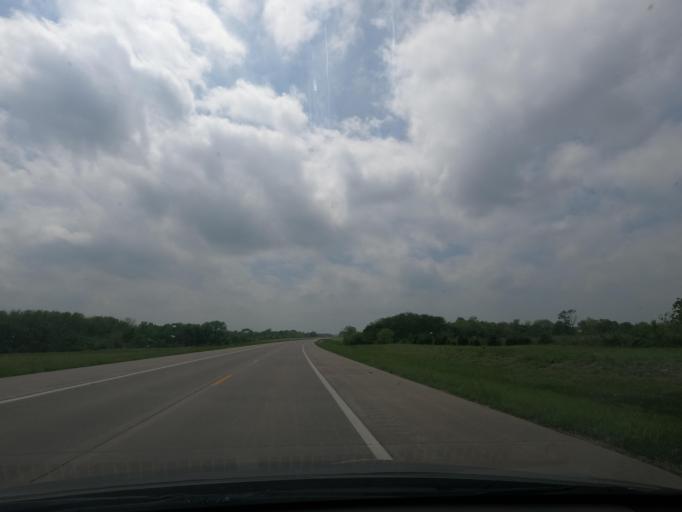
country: US
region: Kansas
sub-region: Labette County
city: Parsons
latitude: 37.3495
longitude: -95.3247
